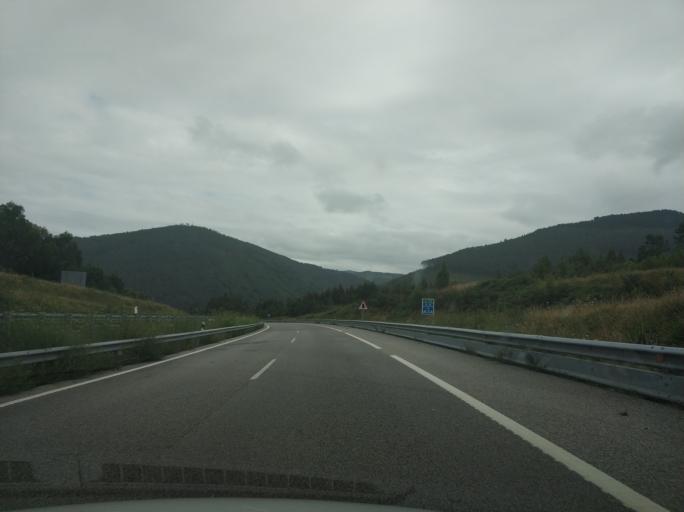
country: ES
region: Asturias
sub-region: Province of Asturias
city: Cudillero
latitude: 43.5575
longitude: -6.2063
